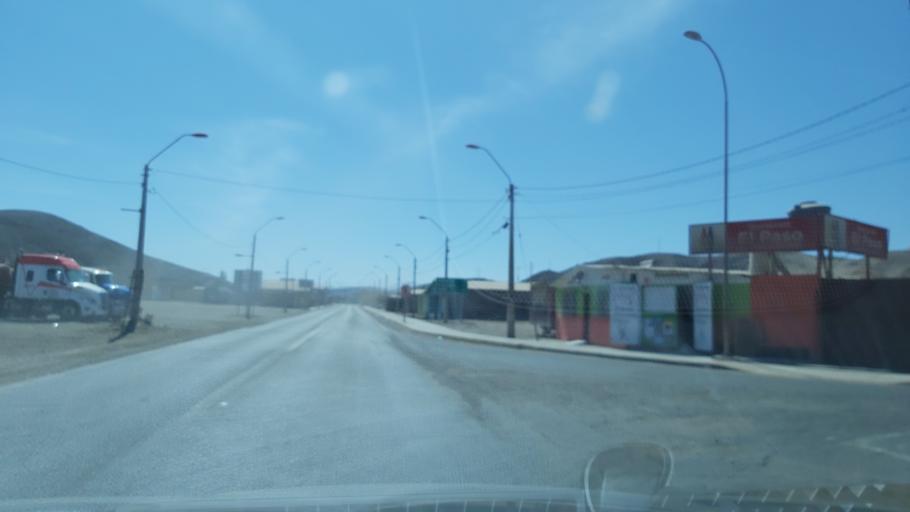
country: CL
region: Atacama
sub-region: Provincia de Chanaral
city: Diego de Almagro
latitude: -26.3914
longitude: -70.0410
